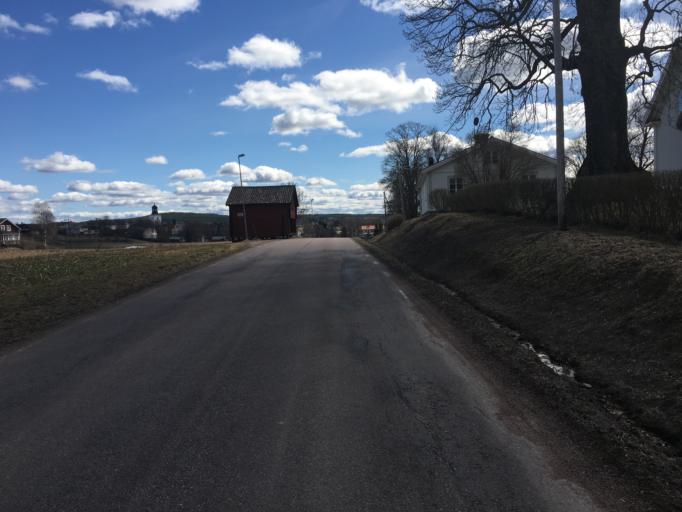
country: SE
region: Gaevleborg
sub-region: Hofors Kommun
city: Hofors
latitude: 60.5128
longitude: 16.4574
